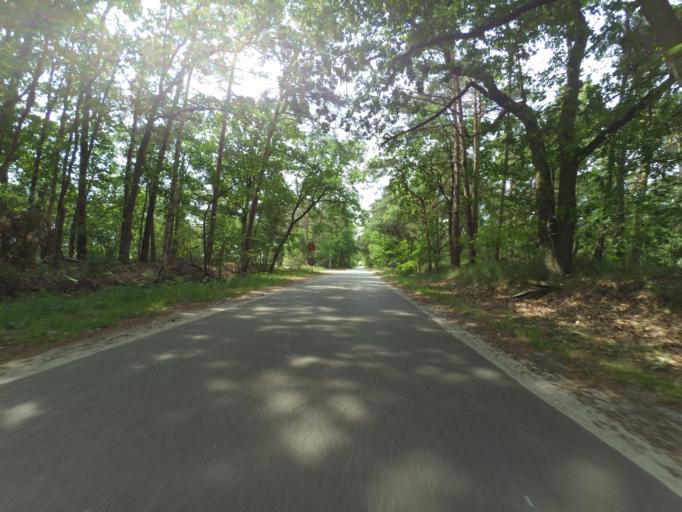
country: BE
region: Flanders
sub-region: Provincie Antwerpen
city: Kalmthout
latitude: 51.4021
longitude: 4.4462
